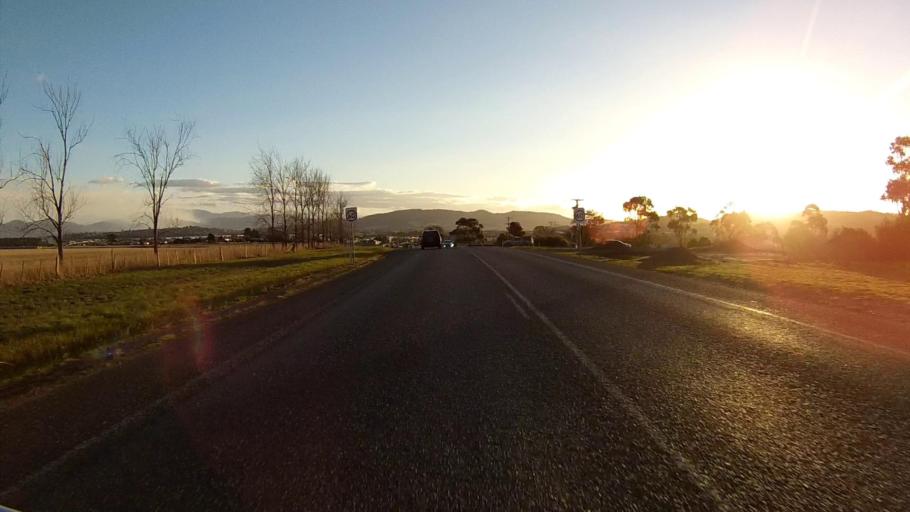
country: AU
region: Tasmania
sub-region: Sorell
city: Sorell
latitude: -42.7815
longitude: 147.5777
